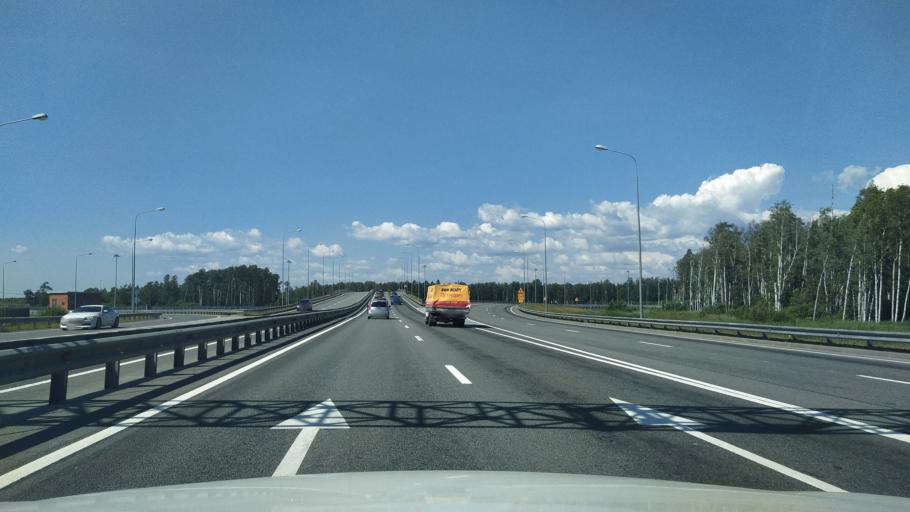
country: RU
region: St.-Petersburg
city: Levashovo
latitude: 60.0725
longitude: 30.1832
